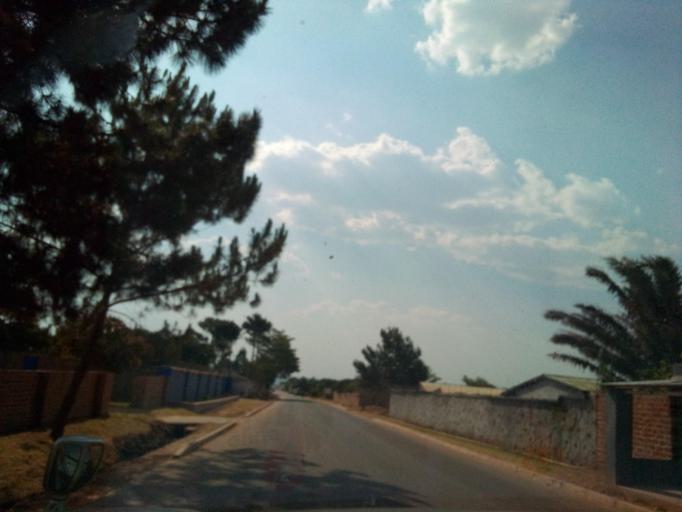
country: ZM
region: Northern
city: Mpika
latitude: -11.8457
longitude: 31.4482
